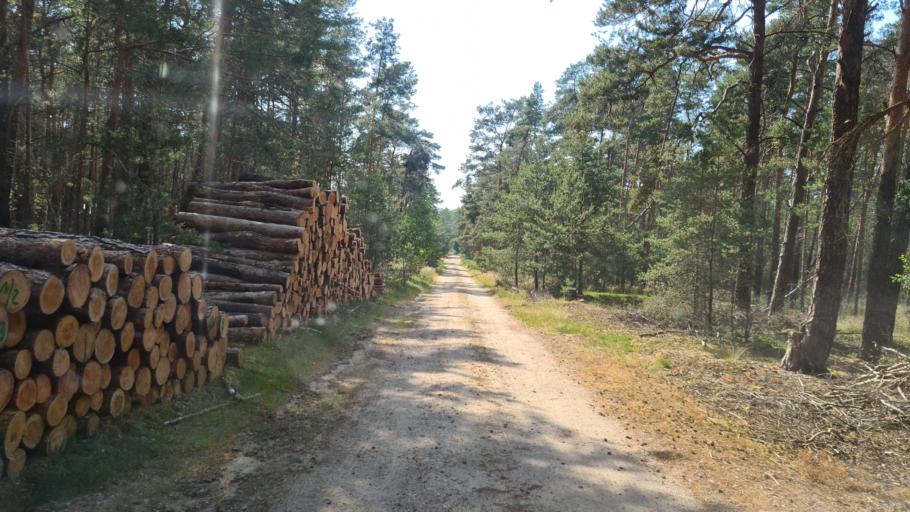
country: DE
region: Brandenburg
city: Schilda
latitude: 51.6342
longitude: 13.3908
